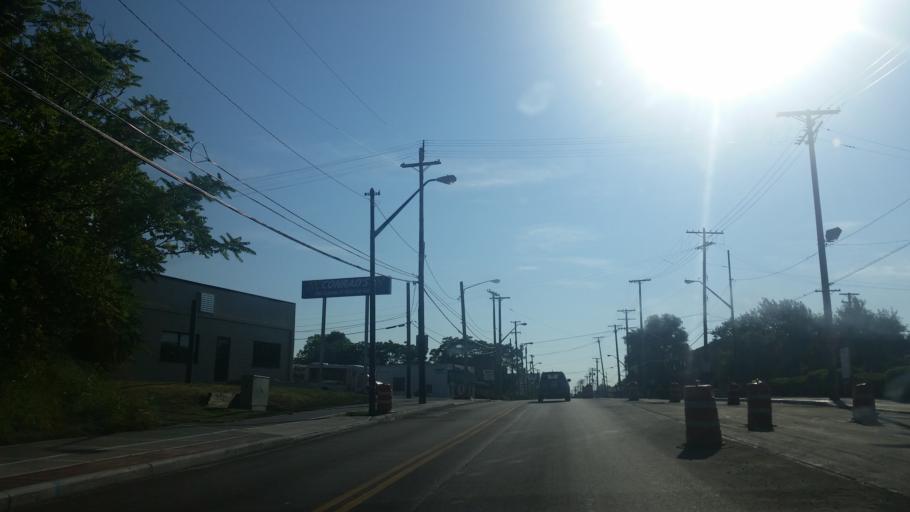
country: US
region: Ohio
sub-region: Cuyahoga County
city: Lakewood
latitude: 41.4540
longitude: -81.7958
